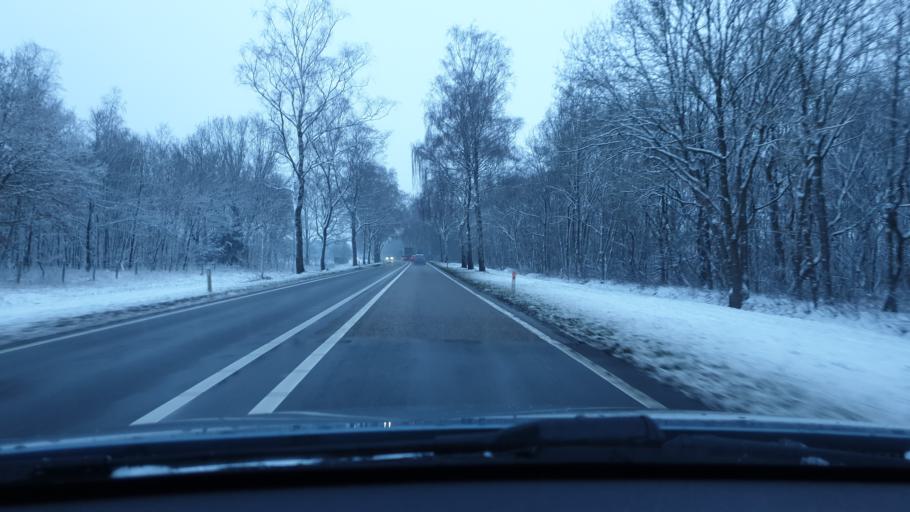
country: NL
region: North Brabant
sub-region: Gemeente Landerd
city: Reek
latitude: 51.7309
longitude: 5.6690
